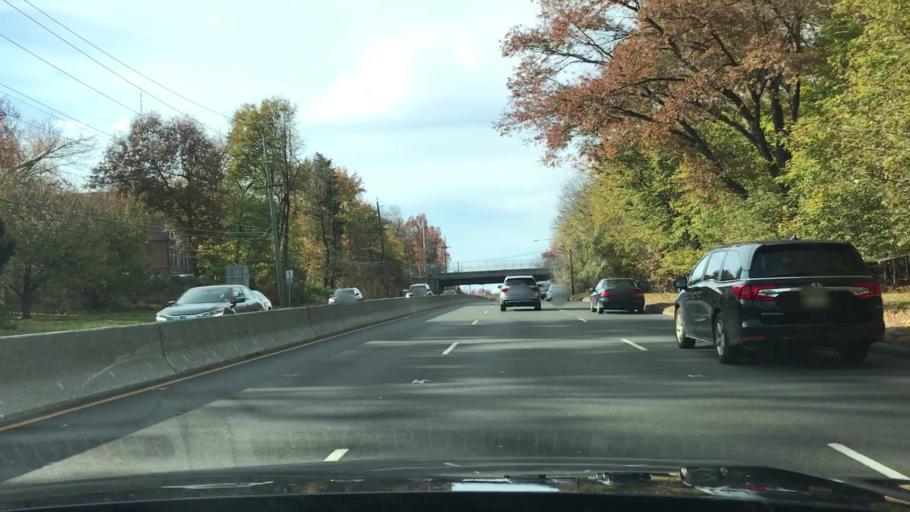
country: US
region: New Jersey
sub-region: Bergen County
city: Teaneck
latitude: 40.8914
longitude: -74.0060
